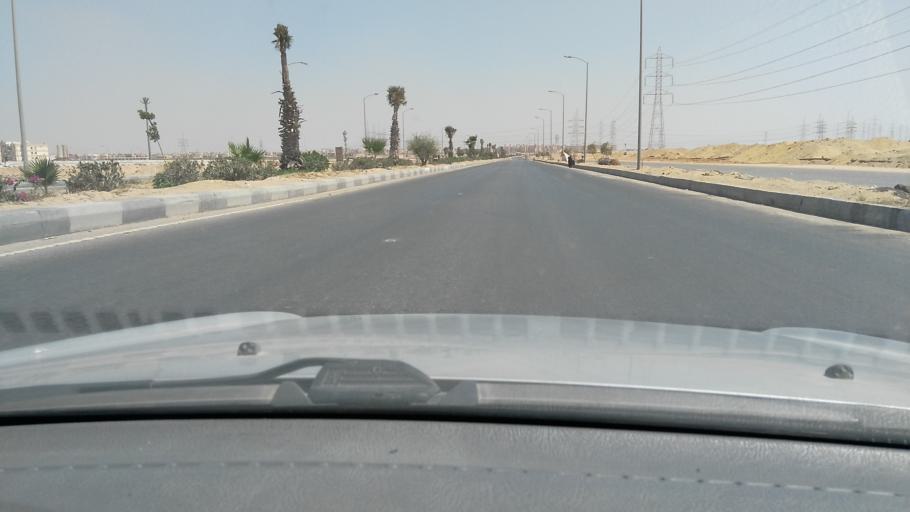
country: EG
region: Al Jizah
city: Madinat Sittah Uktubar
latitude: 29.9387
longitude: 30.9466
